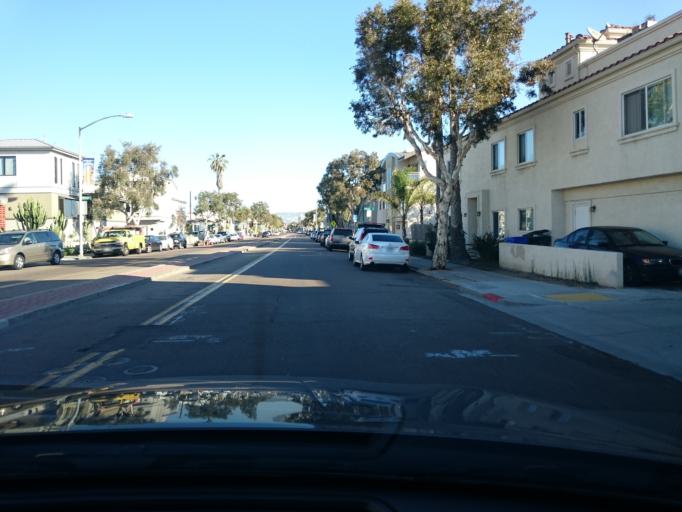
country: US
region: California
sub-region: San Diego County
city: La Jolla
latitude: 32.7790
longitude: -117.2526
